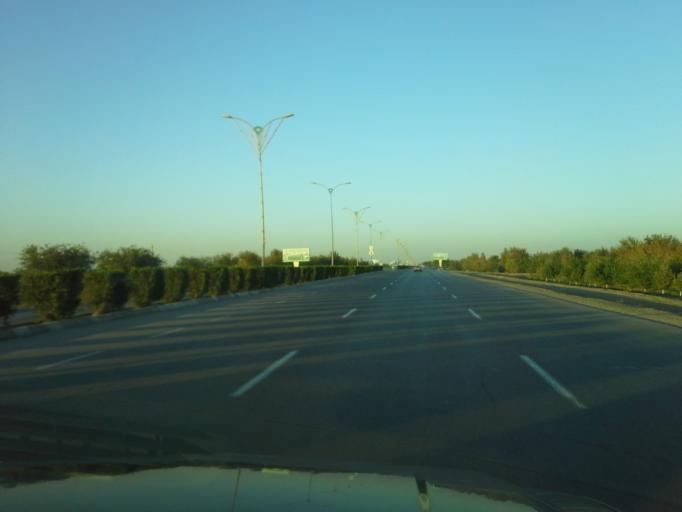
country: TM
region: Dasoguz
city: Dasoguz
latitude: 41.7980
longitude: 59.8935
